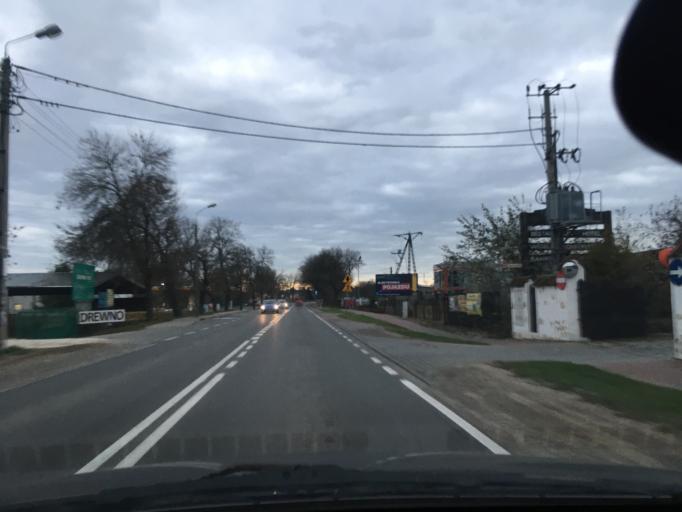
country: PL
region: Masovian Voivodeship
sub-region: Powiat piaseczynski
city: Lesznowola
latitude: 52.0965
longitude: 20.9204
